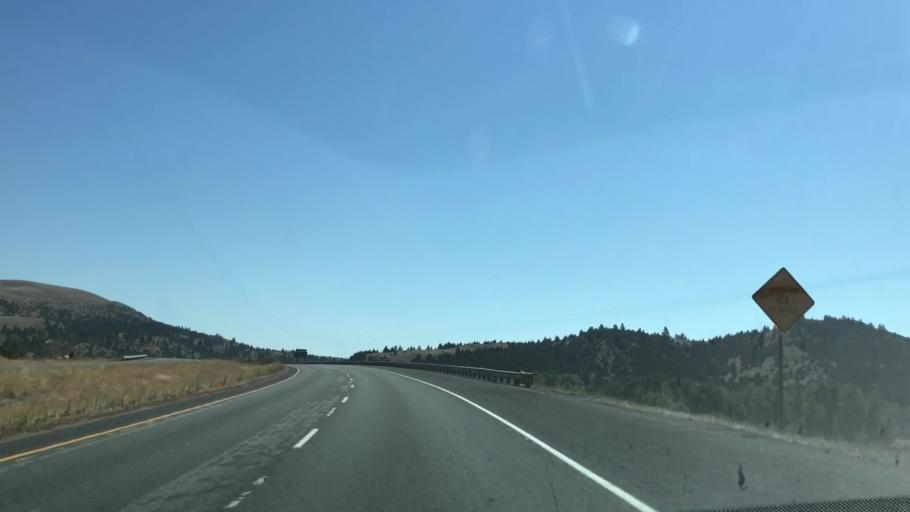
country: US
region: Montana
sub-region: Powell County
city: Deer Lodge
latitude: 46.5570
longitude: -112.8774
